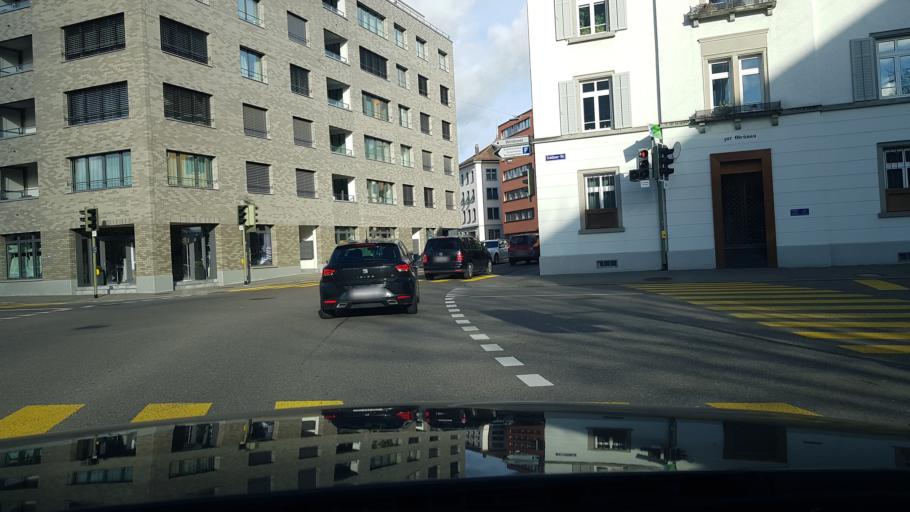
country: CH
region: Zurich
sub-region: Bezirk Winterthur
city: Stadt Winterthur (Kreis 1) / Neuwiesen
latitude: 47.5000
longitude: 8.7190
